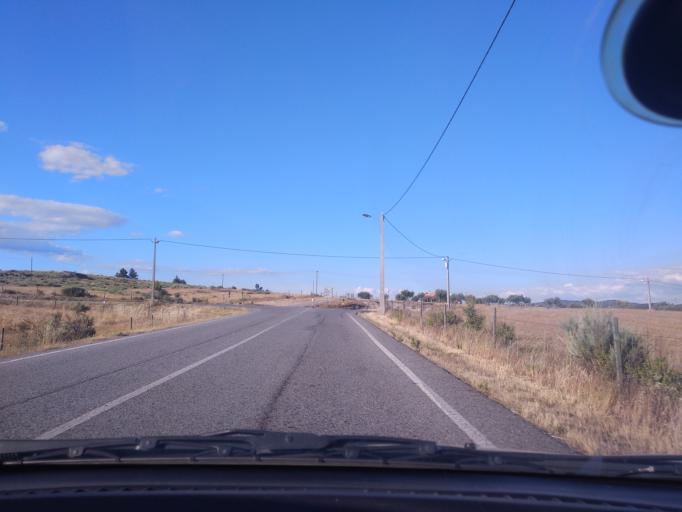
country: PT
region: Castelo Branco
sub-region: Covilha
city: Teixoso
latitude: 40.2525
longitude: -7.3824
